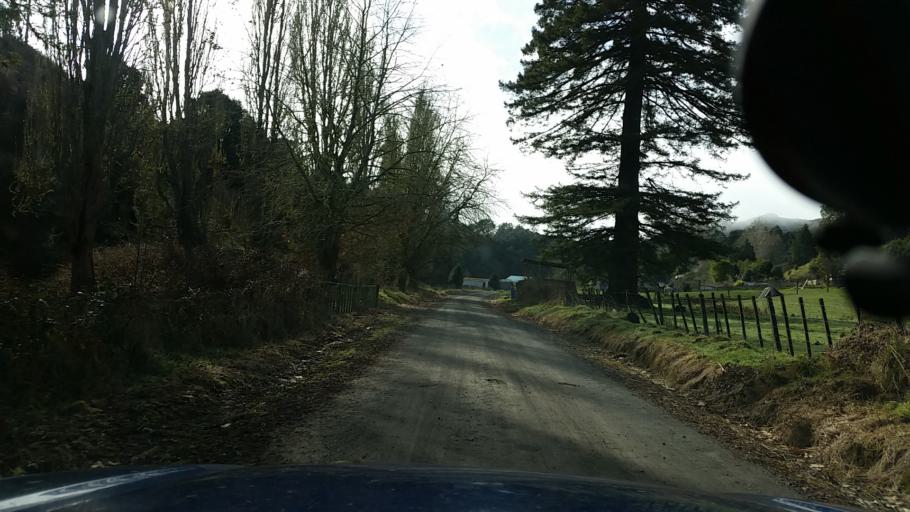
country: NZ
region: Taranaki
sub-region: New Plymouth District
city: Waitara
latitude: -39.0338
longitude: 174.7983
